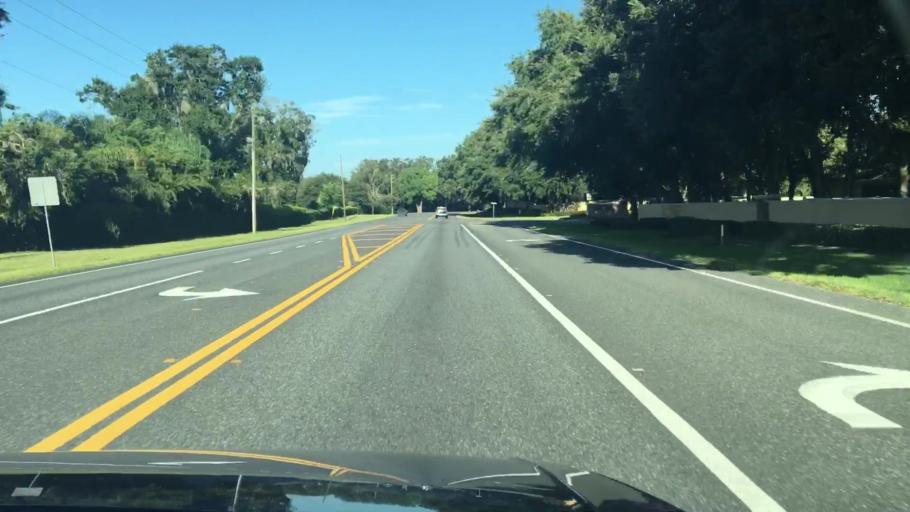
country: US
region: Florida
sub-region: Lake County
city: Eustis
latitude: 28.8513
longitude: -81.6393
